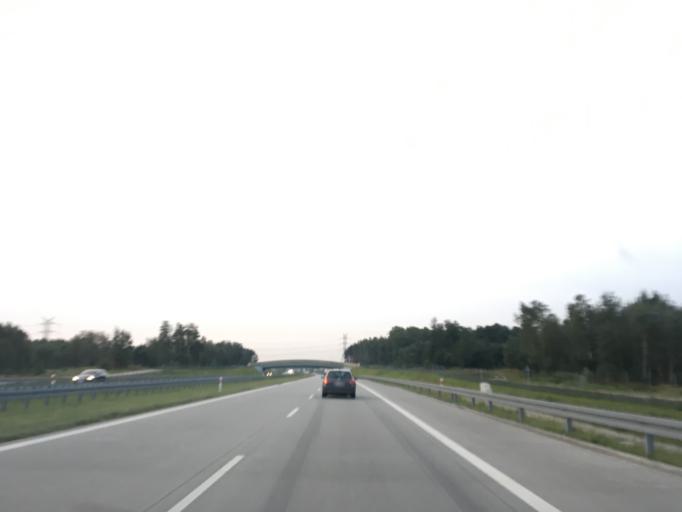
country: PL
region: Lodz Voivodeship
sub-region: Powiat lodzki wschodni
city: Tuszyn
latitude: 51.6089
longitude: 19.5735
